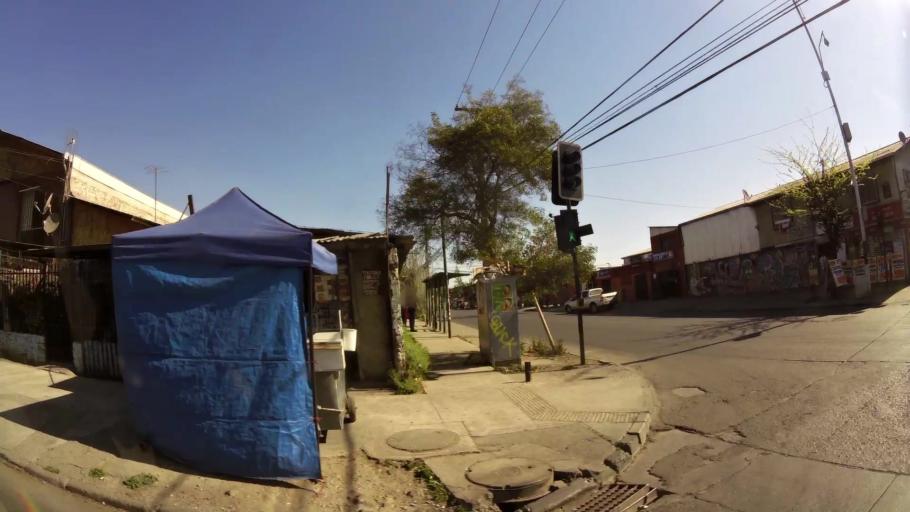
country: CL
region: Santiago Metropolitan
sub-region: Provincia de Maipo
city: San Bernardo
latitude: -33.5197
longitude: -70.6956
